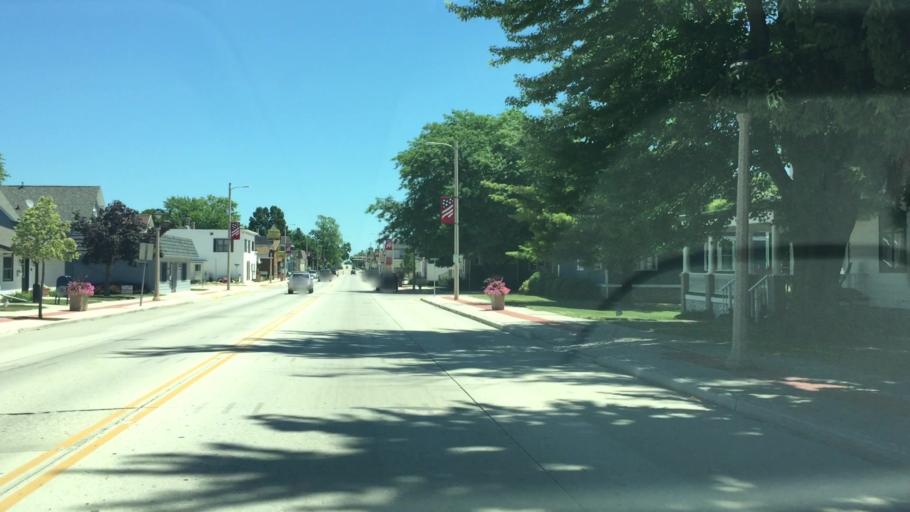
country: US
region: Wisconsin
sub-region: Calumet County
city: New Holstein
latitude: 43.9497
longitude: -88.0890
